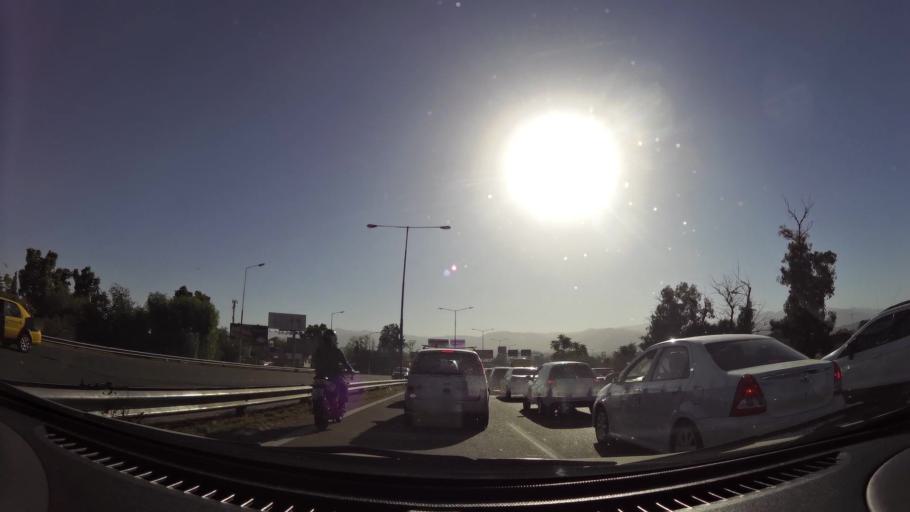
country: AR
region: Mendoza
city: Mendoza
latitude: -32.8972
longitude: -68.8264
